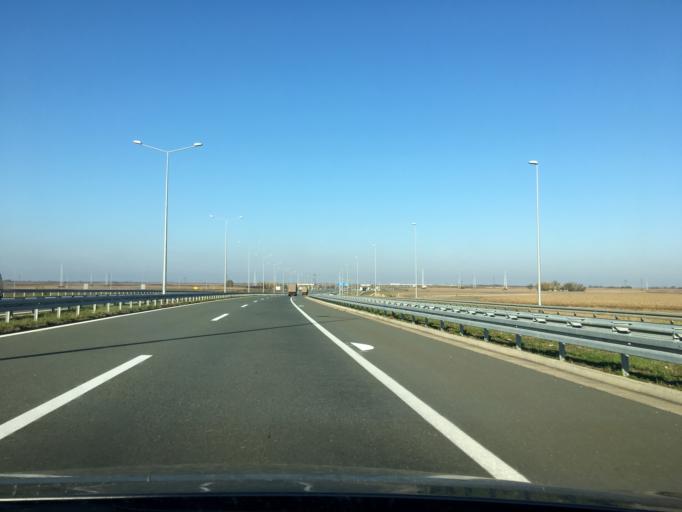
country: RS
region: Autonomna Pokrajina Vojvodina
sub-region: Juznobacki Okrug
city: Novi Sad
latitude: 45.3096
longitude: 19.8068
